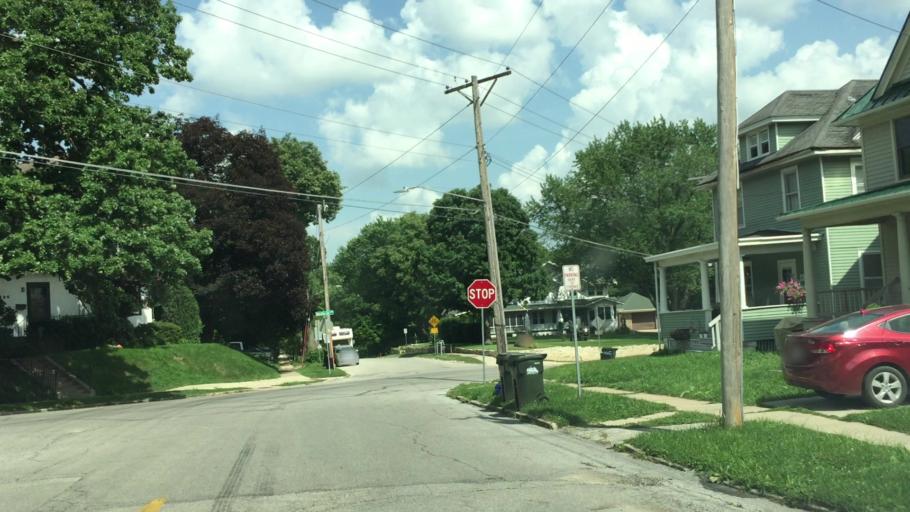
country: US
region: Iowa
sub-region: Johnson County
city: Iowa City
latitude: 41.6589
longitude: -91.5183
